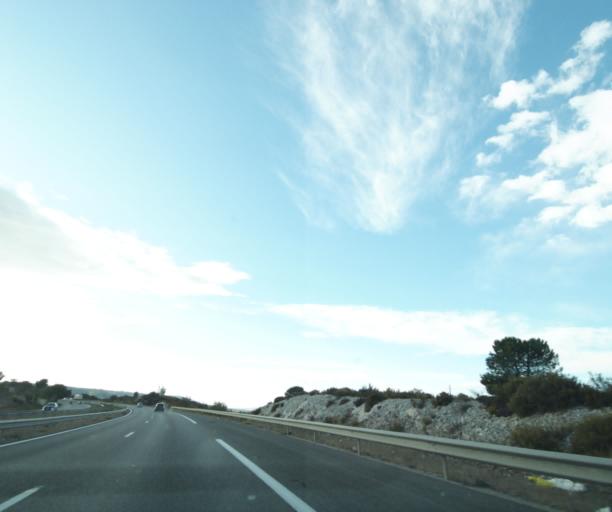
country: FR
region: Provence-Alpes-Cote d'Azur
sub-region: Departement des Bouches-du-Rhone
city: Gignac-la-Nerthe
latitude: 43.3809
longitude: 5.2126
